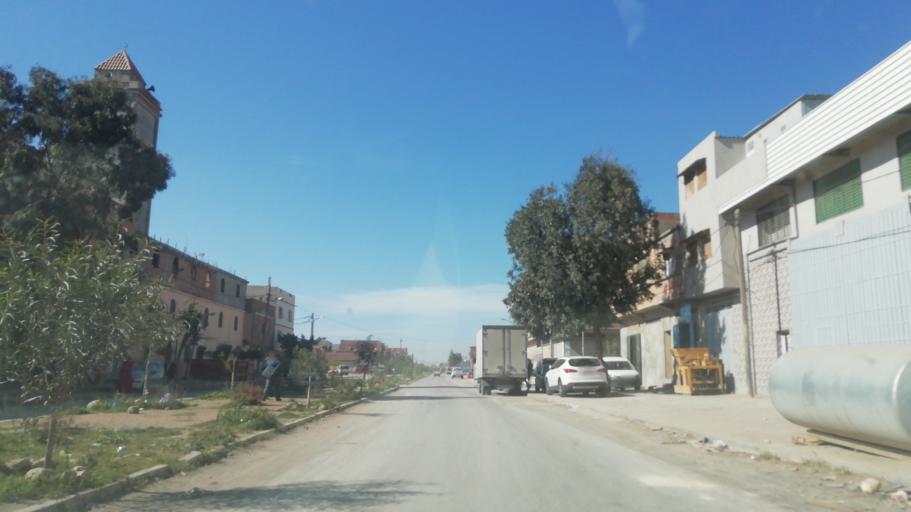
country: DZ
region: Oran
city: Es Senia
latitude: 35.6457
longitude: -0.5780
